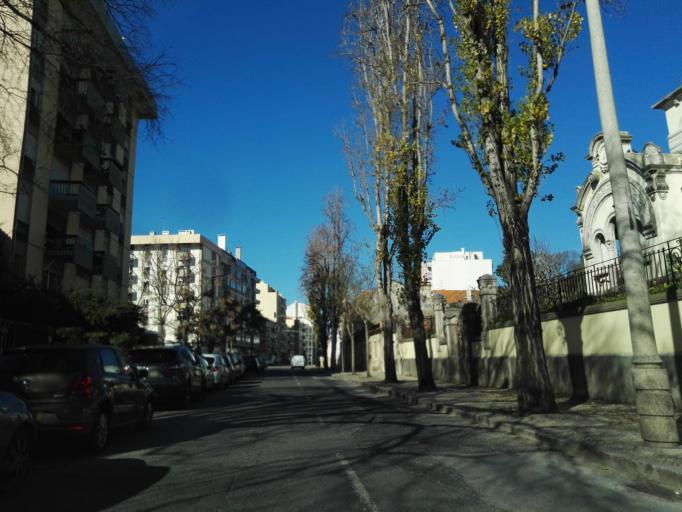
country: PT
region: Lisbon
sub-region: Odivelas
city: Olival do Basto
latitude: 38.7620
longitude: -9.1562
